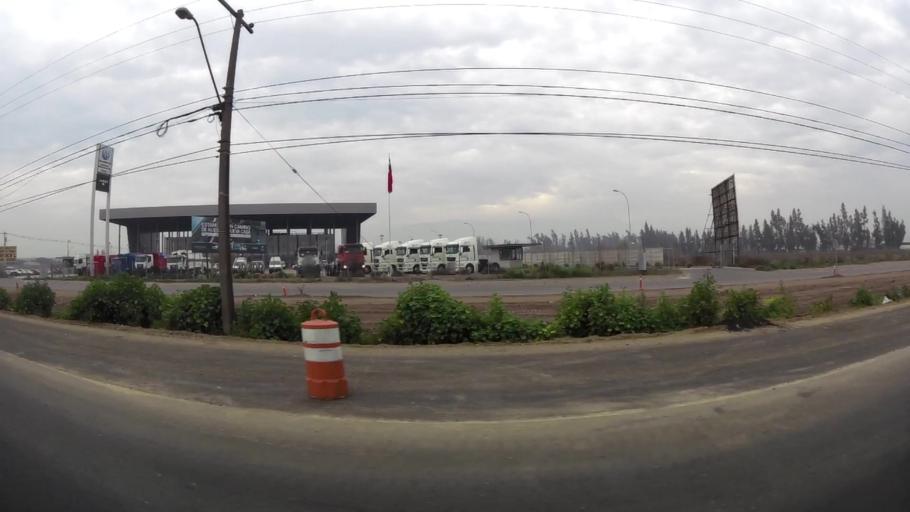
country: CL
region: Santiago Metropolitan
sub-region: Provincia de Chacabuco
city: Chicureo Abajo
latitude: -33.2806
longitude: -70.7385
